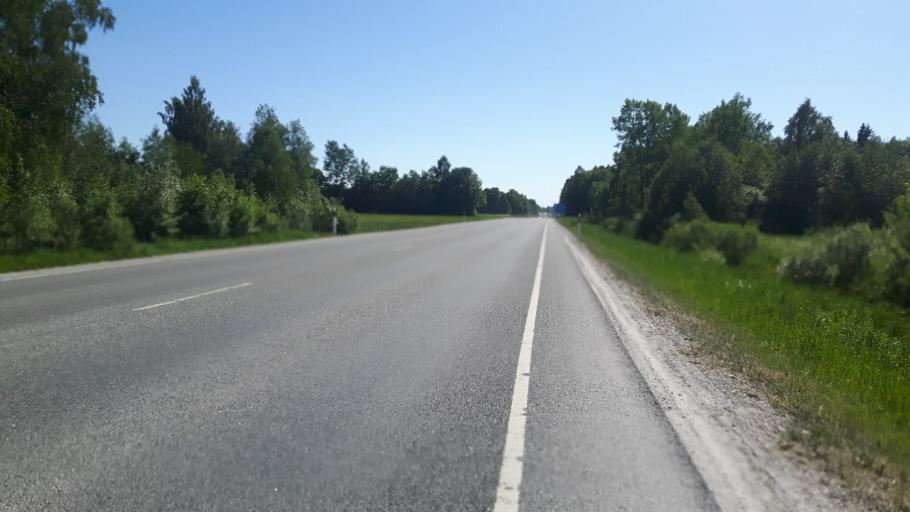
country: EE
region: Raplamaa
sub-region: Rapla vald
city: Rapla
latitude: 59.0198
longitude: 24.8076
